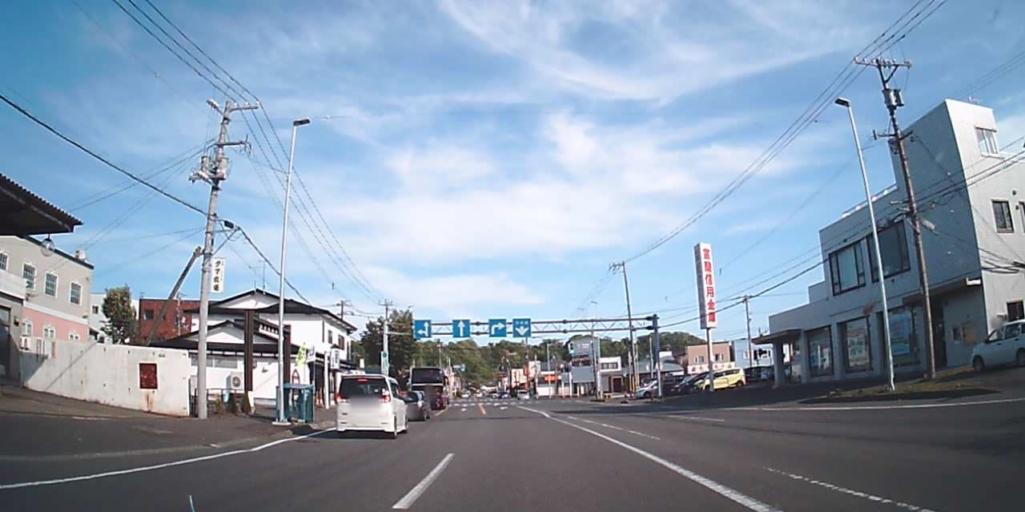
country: JP
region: Hokkaido
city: Shiraoi
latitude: 42.4551
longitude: 141.1773
